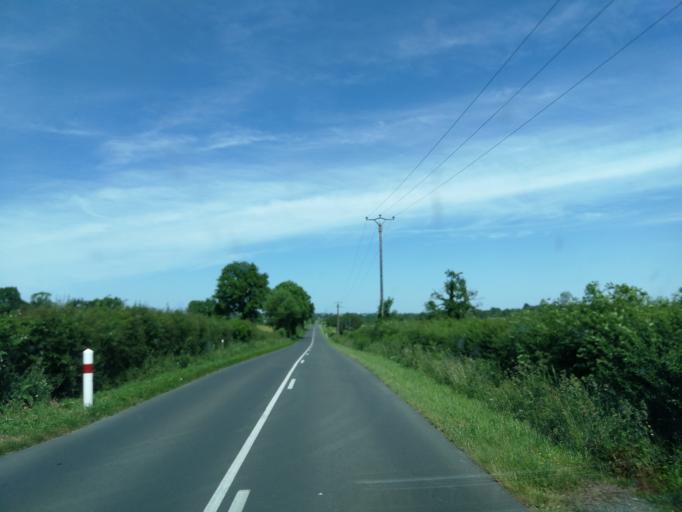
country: FR
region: Poitou-Charentes
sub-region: Departement des Deux-Sevres
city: Courlay
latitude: 46.8115
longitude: -0.5461
